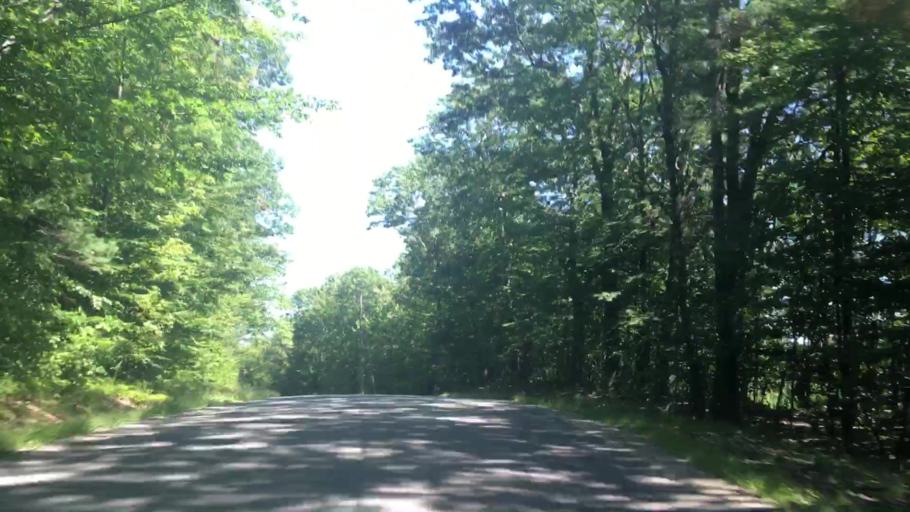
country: US
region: Maine
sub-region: Androscoggin County
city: Sabattus
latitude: 44.1221
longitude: -70.0453
